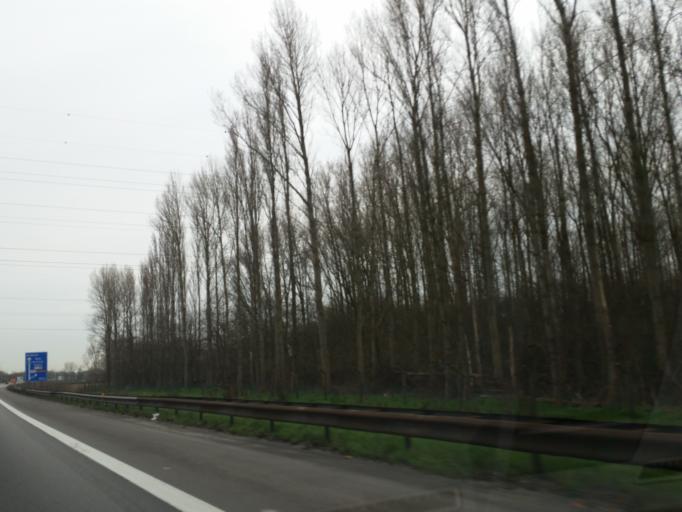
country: BE
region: Flanders
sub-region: Provincie Antwerpen
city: Kontich
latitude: 51.1112
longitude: 4.4317
